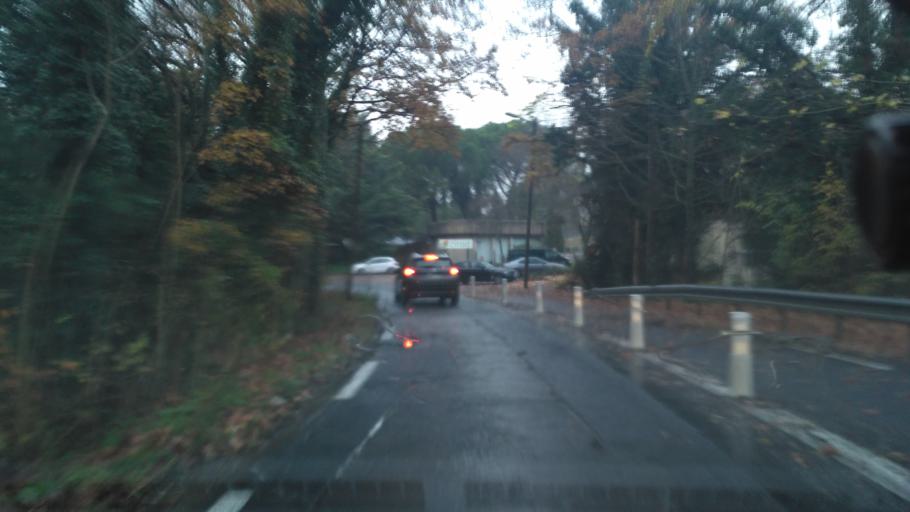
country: FR
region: Languedoc-Roussillon
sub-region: Departement de l'Herault
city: Clapiers
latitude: 43.6482
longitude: 3.8686
